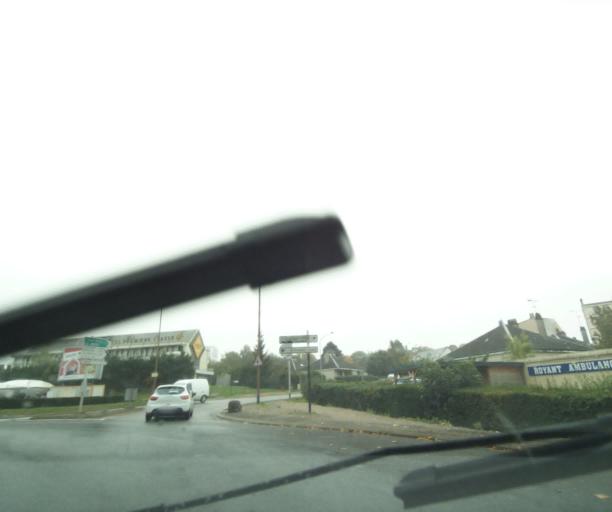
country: FR
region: Centre
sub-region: Departement d'Eure-et-Loir
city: Dreux
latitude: 48.7419
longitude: 1.3872
